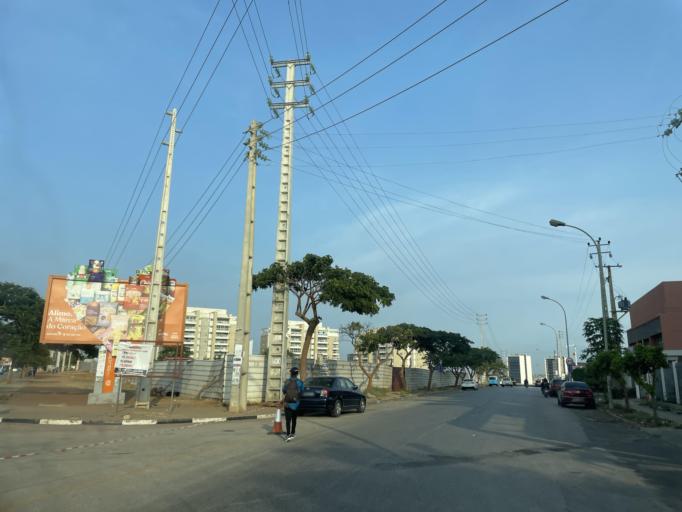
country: AO
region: Luanda
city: Luanda
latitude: -8.9179
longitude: 13.1946
